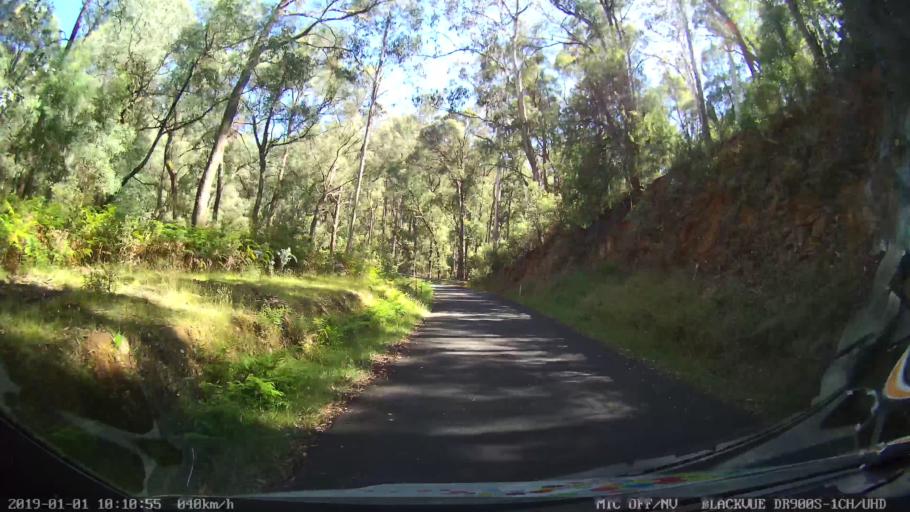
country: AU
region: New South Wales
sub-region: Snowy River
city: Jindabyne
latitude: -36.1381
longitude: 148.1582
